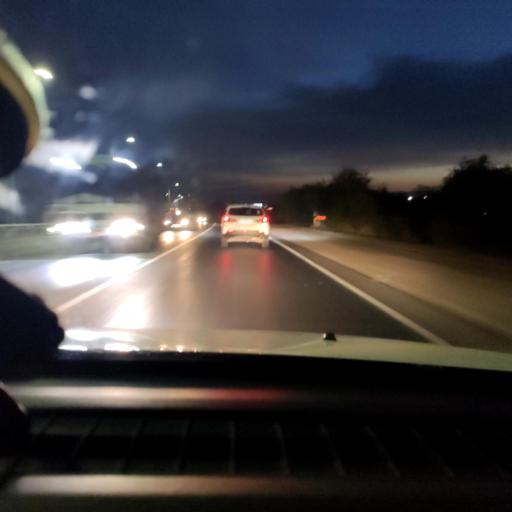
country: RU
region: Samara
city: Samara
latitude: 53.0839
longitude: 50.1382
